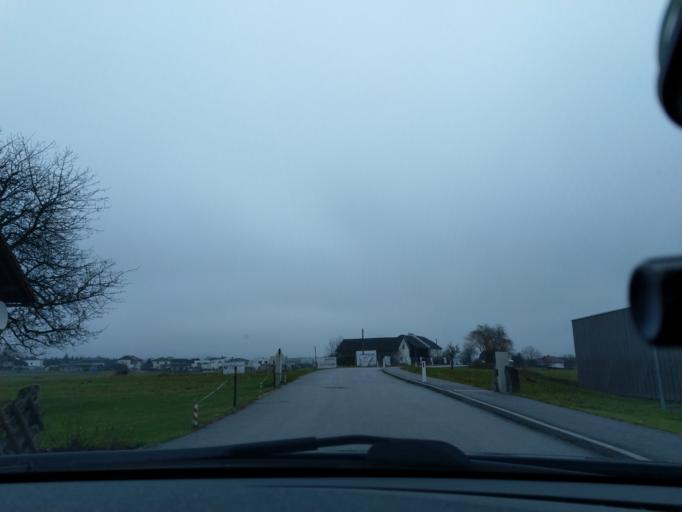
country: AT
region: Upper Austria
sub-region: Politischer Bezirk Urfahr-Umgebung
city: Engerwitzdorf
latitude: 48.3749
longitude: 14.5163
